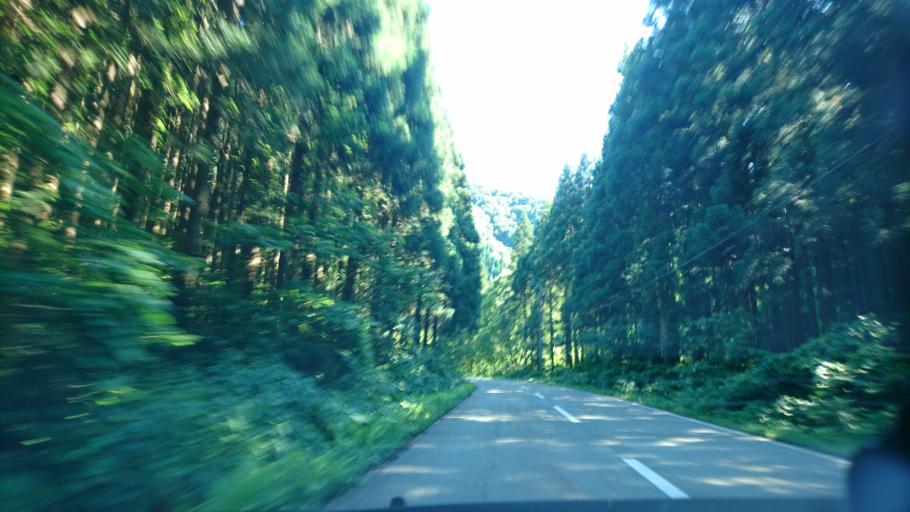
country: JP
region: Akita
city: Kakunodatemachi
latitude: 39.7152
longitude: 140.6191
